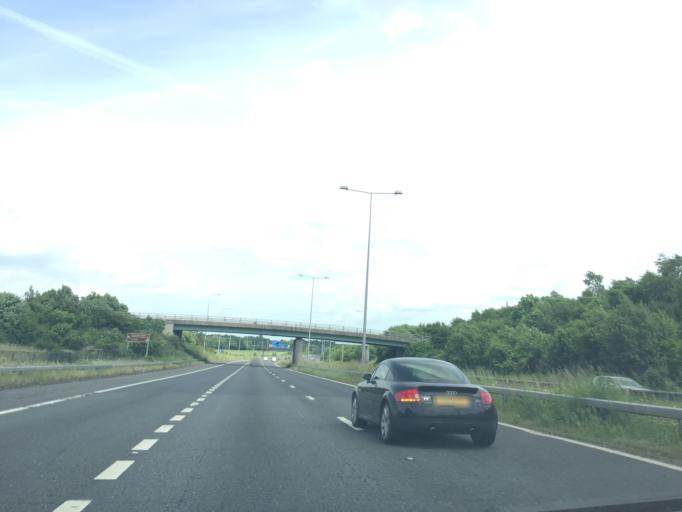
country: GB
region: England
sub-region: Kent
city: Boxley
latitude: 51.3309
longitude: 0.5701
